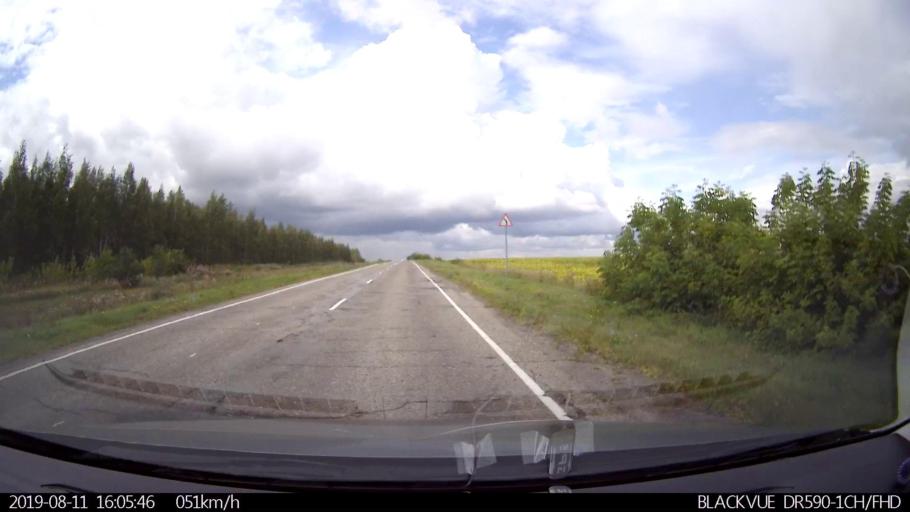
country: RU
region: Ulyanovsk
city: Ignatovka
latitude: 53.9631
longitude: 47.6491
